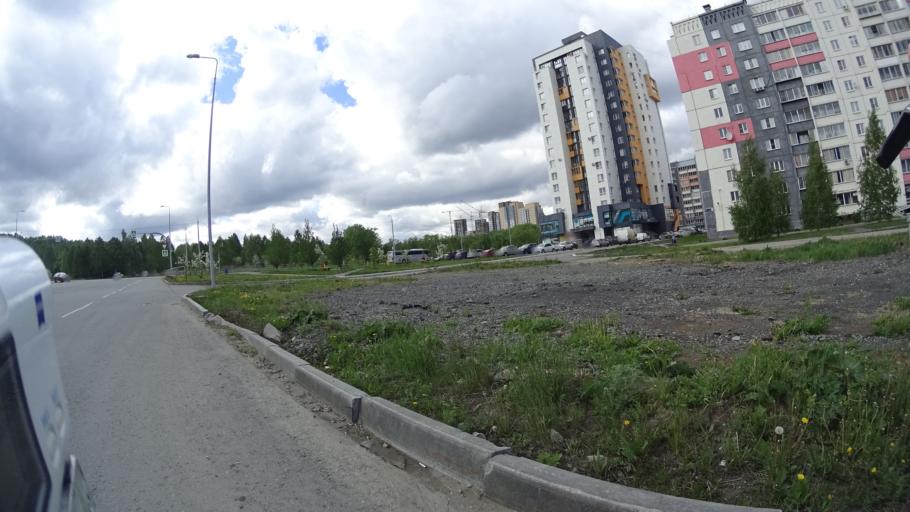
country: RU
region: Chelyabinsk
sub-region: Gorod Chelyabinsk
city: Chelyabinsk
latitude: 55.1634
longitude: 61.2872
